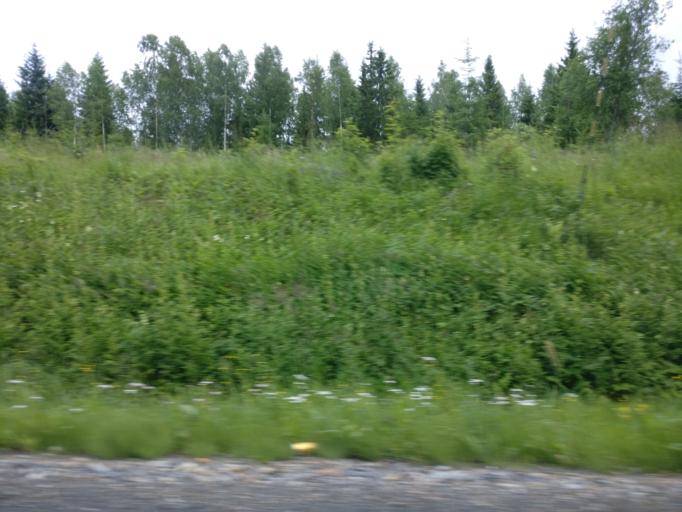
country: FI
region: Northern Savo
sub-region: Varkaus
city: Leppaevirta
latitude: 62.6110
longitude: 27.6232
